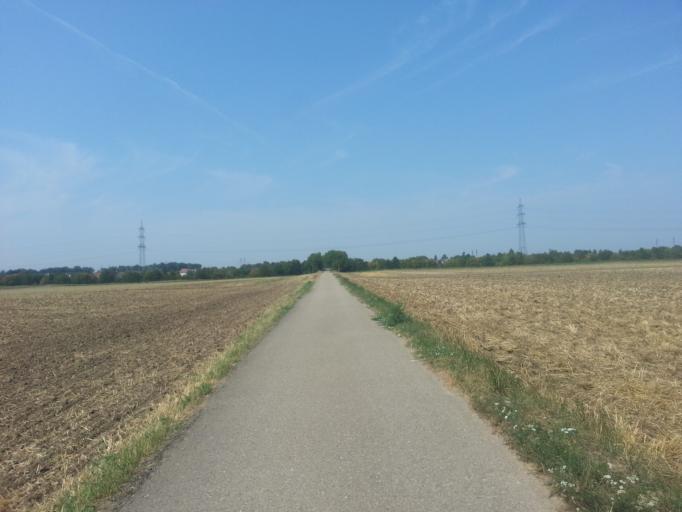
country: DE
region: Baden-Wuerttemberg
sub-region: Karlsruhe Region
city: Ilvesheim
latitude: 49.4538
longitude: 8.5797
